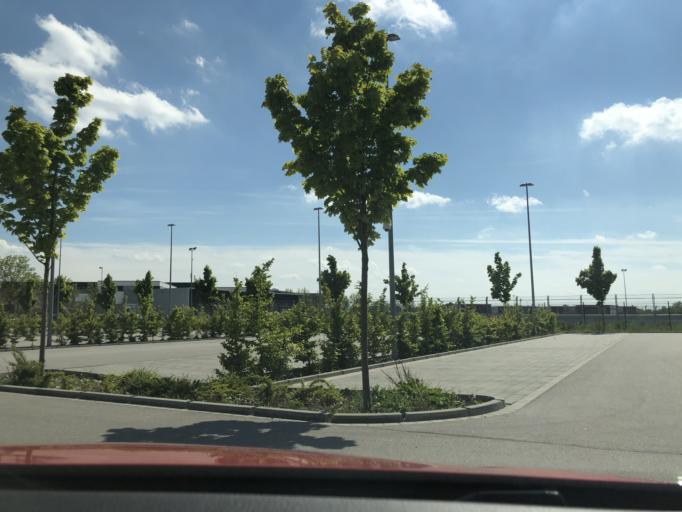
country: DE
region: Bavaria
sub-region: Upper Bavaria
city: Lenting
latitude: 48.7850
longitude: 11.4743
